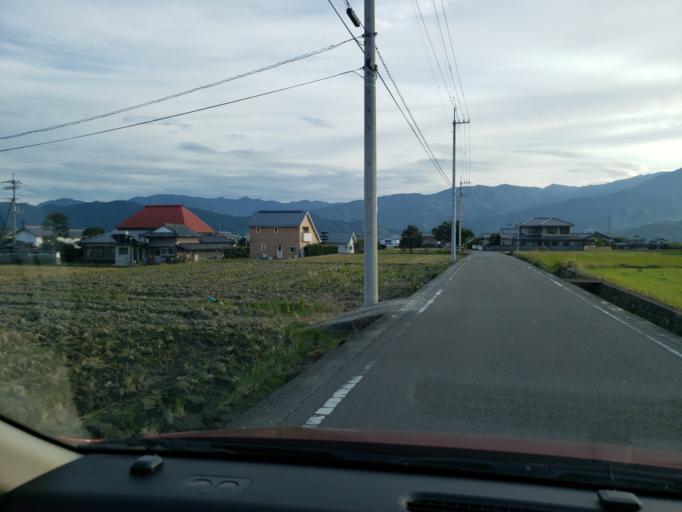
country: JP
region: Tokushima
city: Wakimachi
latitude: 34.0868
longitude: 134.2267
